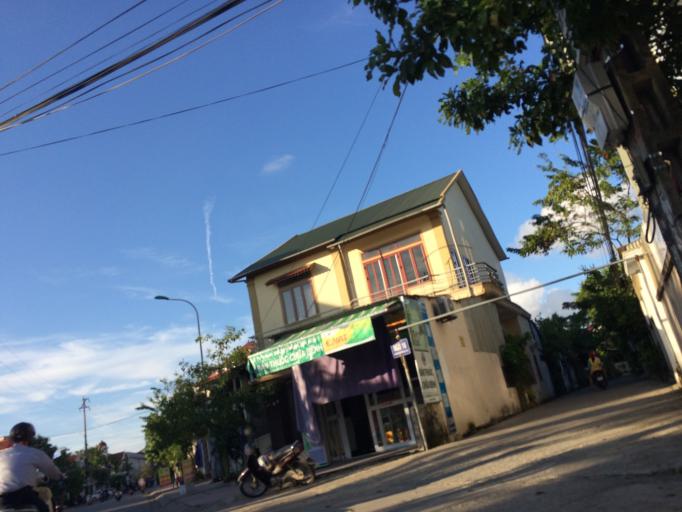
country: VN
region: Ha Tinh
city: Ha Tinh
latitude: 18.3459
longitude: 105.8991
